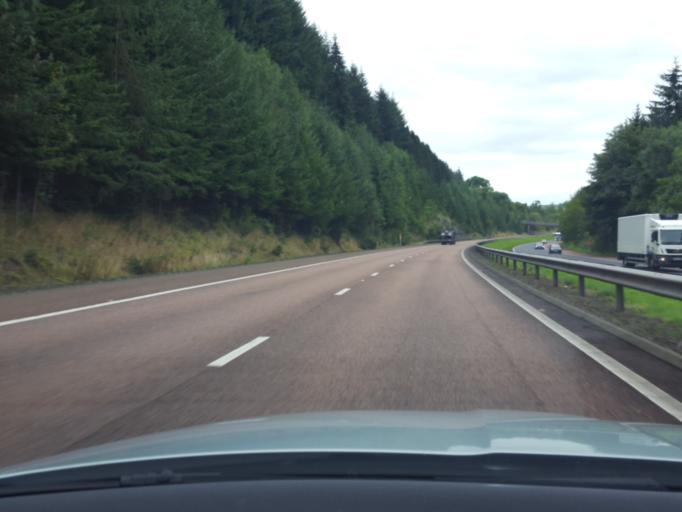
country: GB
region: Scotland
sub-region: Perth and Kinross
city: Bridge of Earn
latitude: 56.3201
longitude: -3.3846
